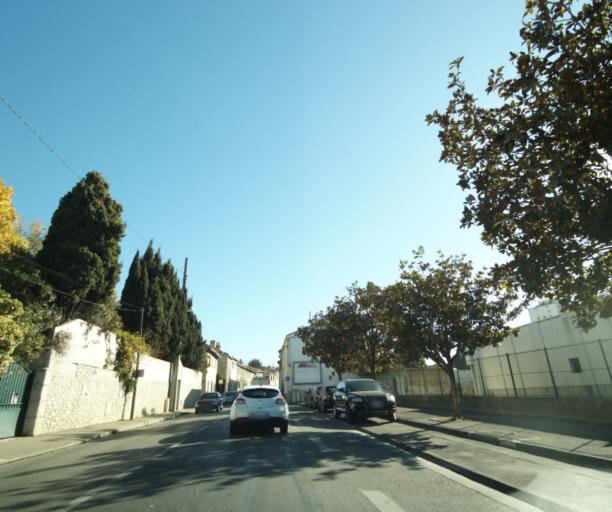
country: FR
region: Provence-Alpes-Cote d'Azur
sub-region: Departement des Bouches-du-Rhone
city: Marseille 14
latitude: 43.3375
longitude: 5.3951
